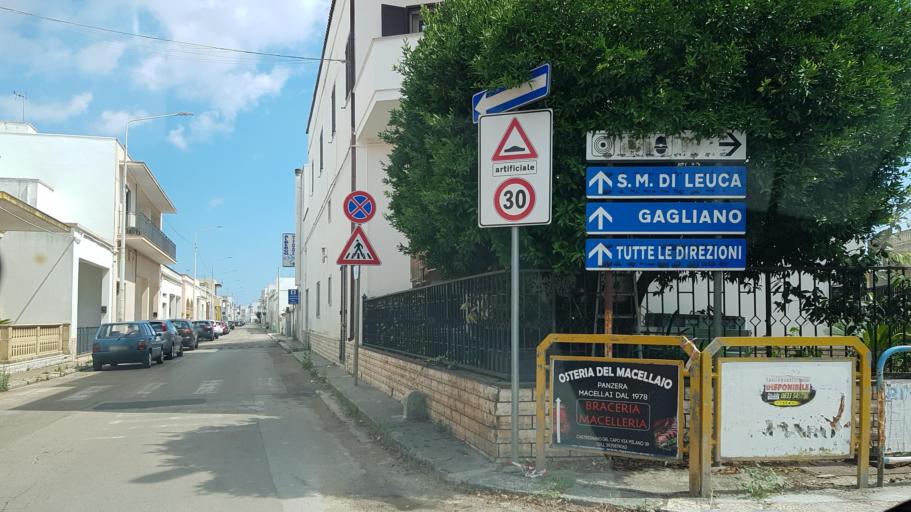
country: IT
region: Apulia
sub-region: Provincia di Lecce
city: Castrignano del Capo
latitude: 39.8377
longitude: 18.3458
